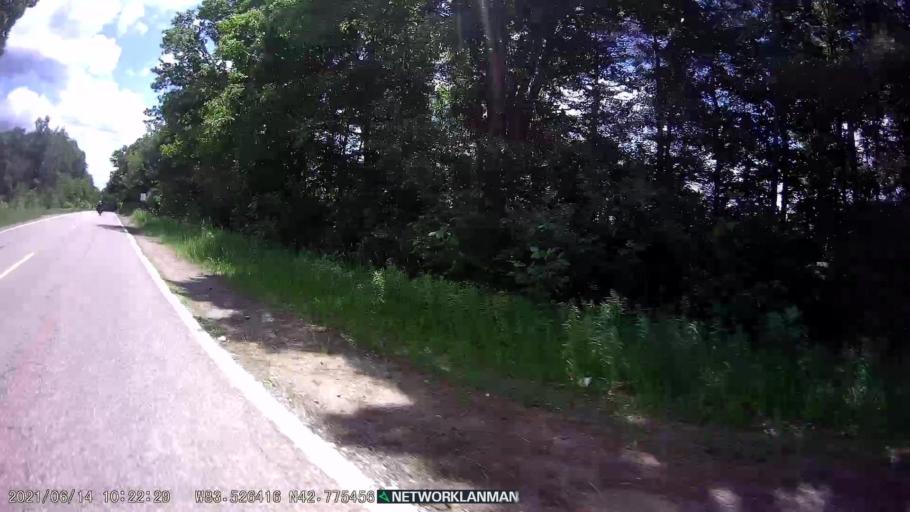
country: US
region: Michigan
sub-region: Oakland County
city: Holly
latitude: 42.7753
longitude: -83.5263
